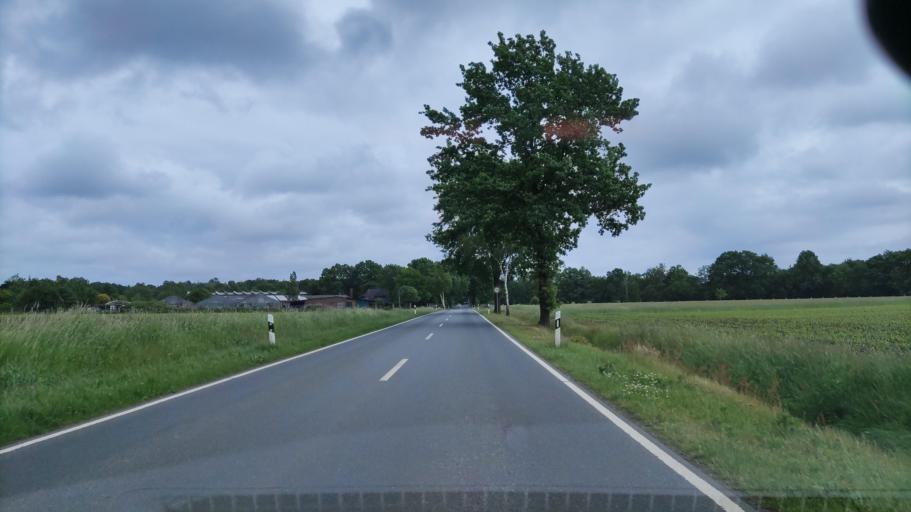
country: DE
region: Lower Saxony
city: Schneverdingen
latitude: 53.1104
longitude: 9.7705
